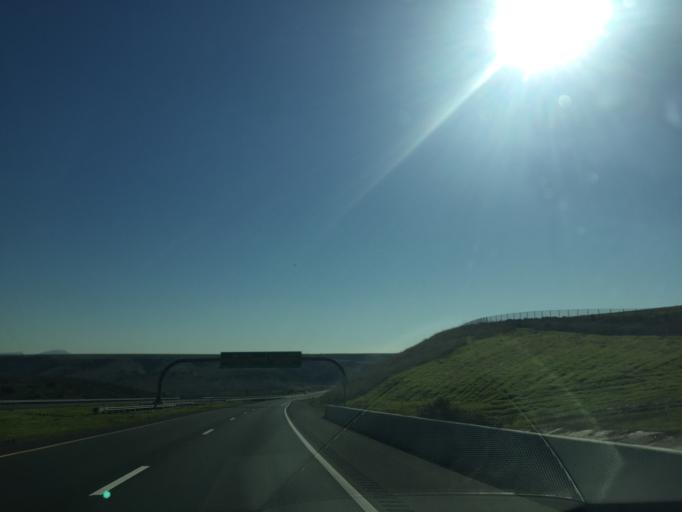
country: US
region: California
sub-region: San Diego County
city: Bonita
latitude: 32.6016
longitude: -116.9645
